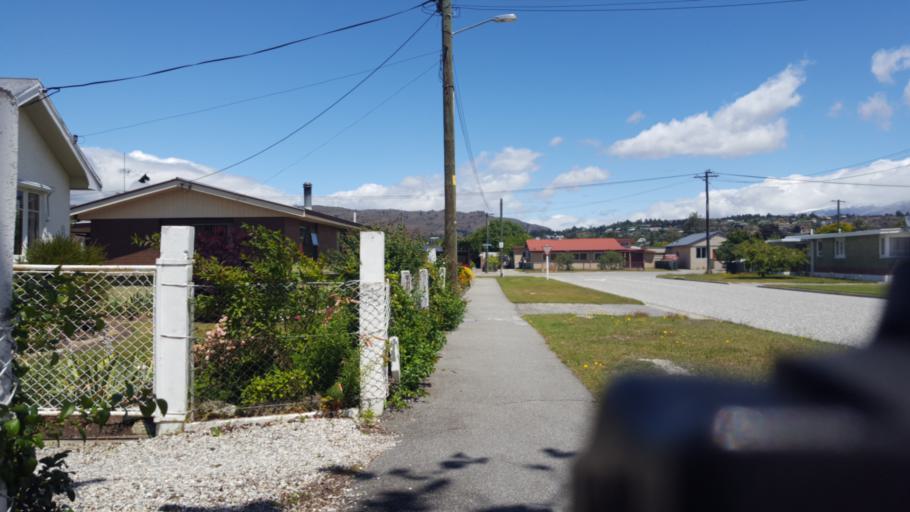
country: NZ
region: Otago
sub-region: Queenstown-Lakes District
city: Wanaka
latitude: -45.2480
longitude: 169.3909
